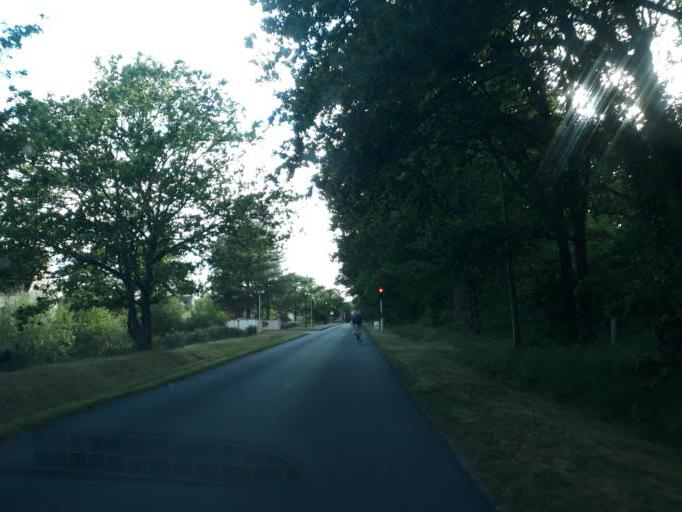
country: FR
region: Centre
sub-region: Departement du Loiret
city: La Ferte-Saint-Aubin
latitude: 47.7244
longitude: 1.9607
